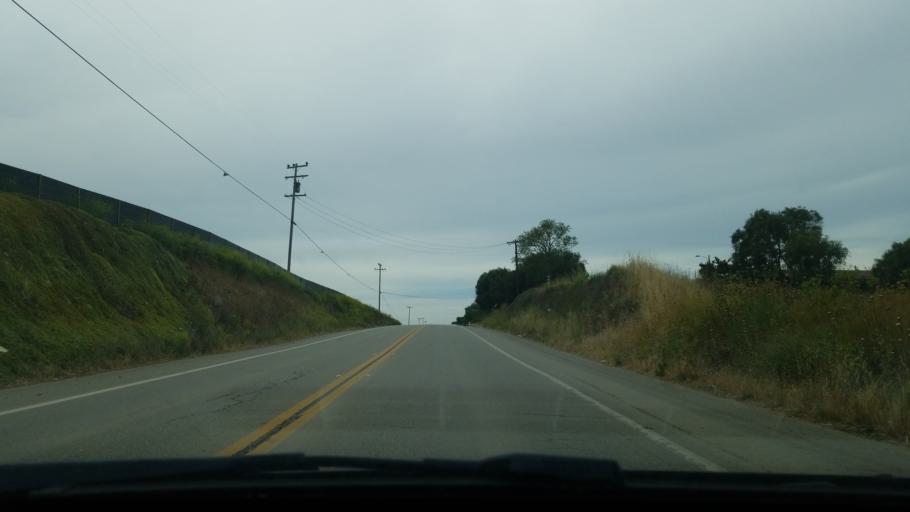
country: US
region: California
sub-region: Santa Barbara County
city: Santa Maria
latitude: 34.9235
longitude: -120.3767
